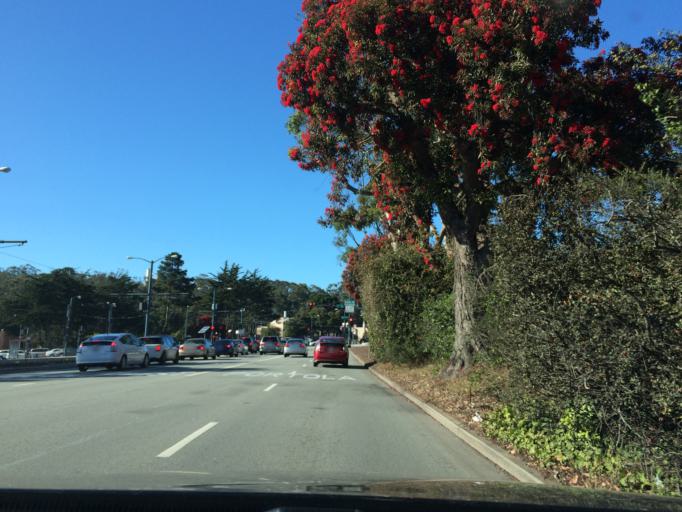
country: US
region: California
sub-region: San Mateo County
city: Daly City
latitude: 37.7337
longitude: -122.4714
